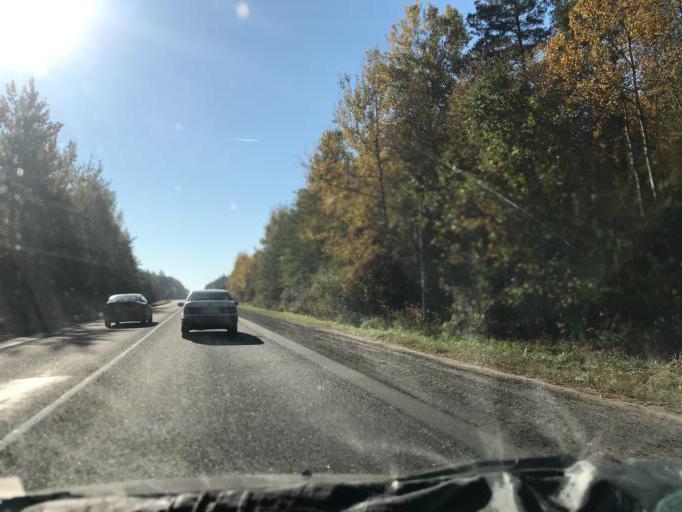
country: BY
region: Mogilev
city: Babruysk
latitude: 53.1692
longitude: 29.0446
